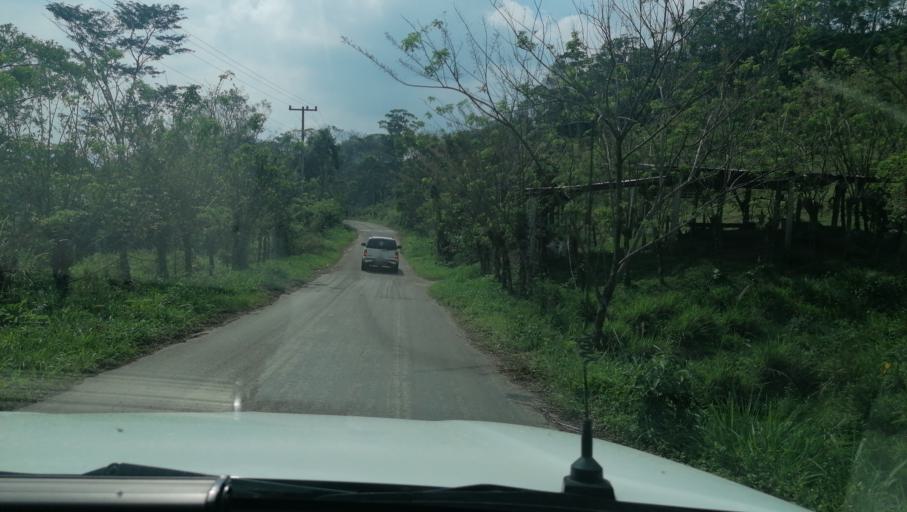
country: MX
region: Chiapas
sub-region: Francisco Leon
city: San Miguel la Sardina
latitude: 17.2341
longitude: -93.3377
